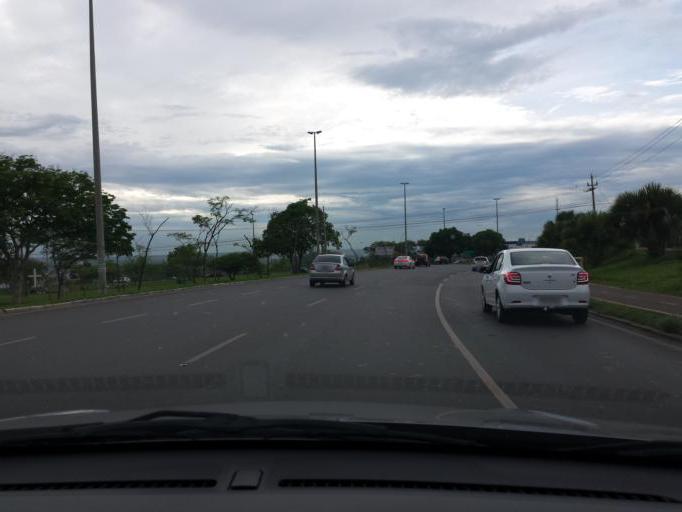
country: BR
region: Federal District
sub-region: Brasilia
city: Brasilia
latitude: -15.8366
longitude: -47.9675
